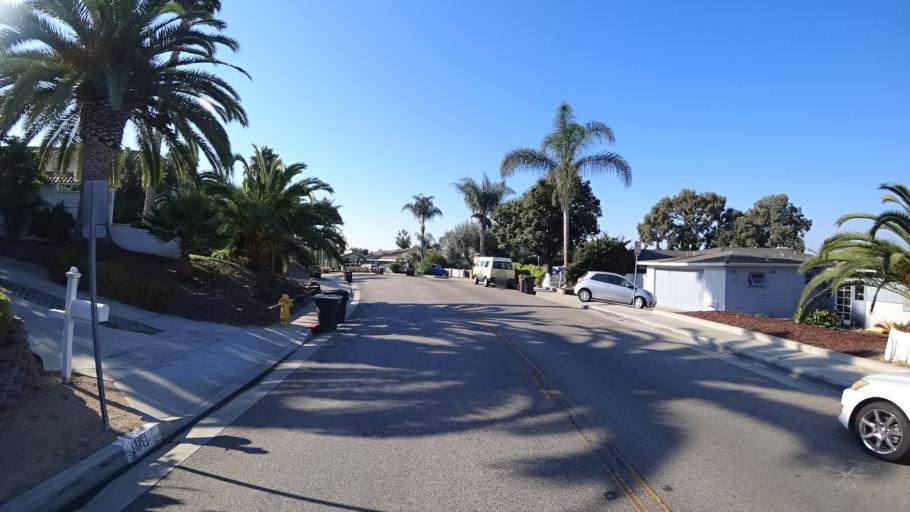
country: US
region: California
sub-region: Orange County
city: San Clemente
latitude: 33.4347
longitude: -117.6157
